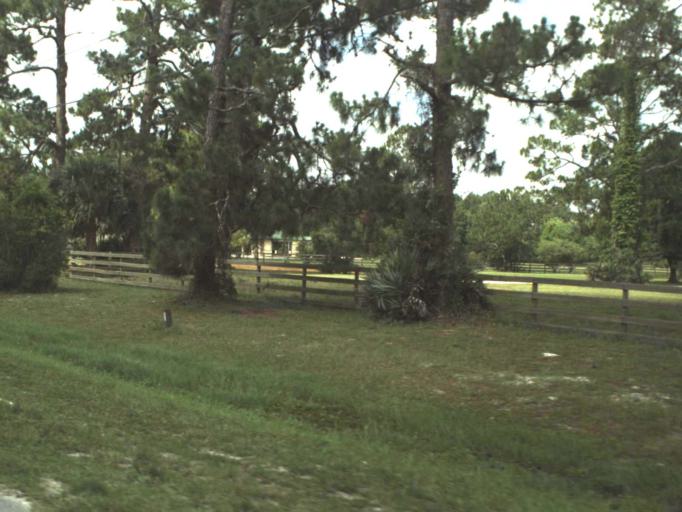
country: US
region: Florida
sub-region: Volusia County
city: Samsula-Spruce Creek
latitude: 29.0070
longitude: -81.0696
